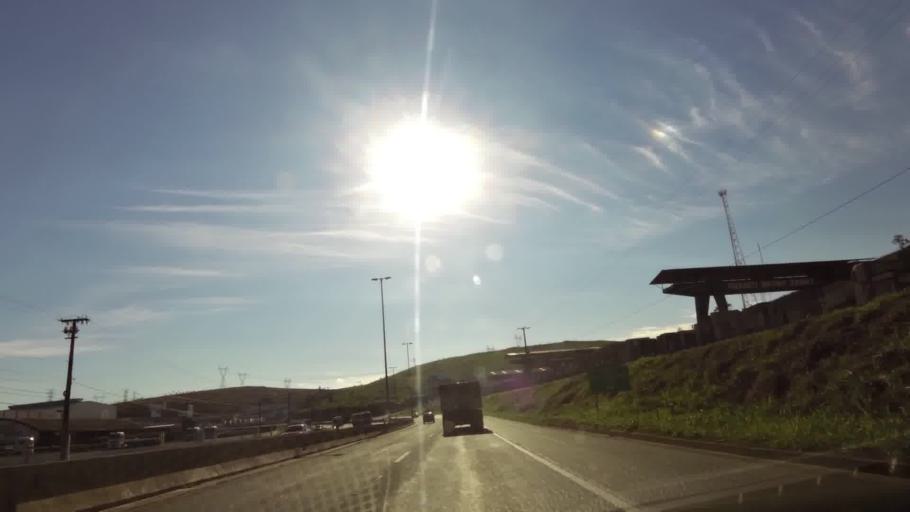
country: BR
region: Espirito Santo
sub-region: Viana
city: Viana
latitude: -20.3769
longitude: -40.4449
